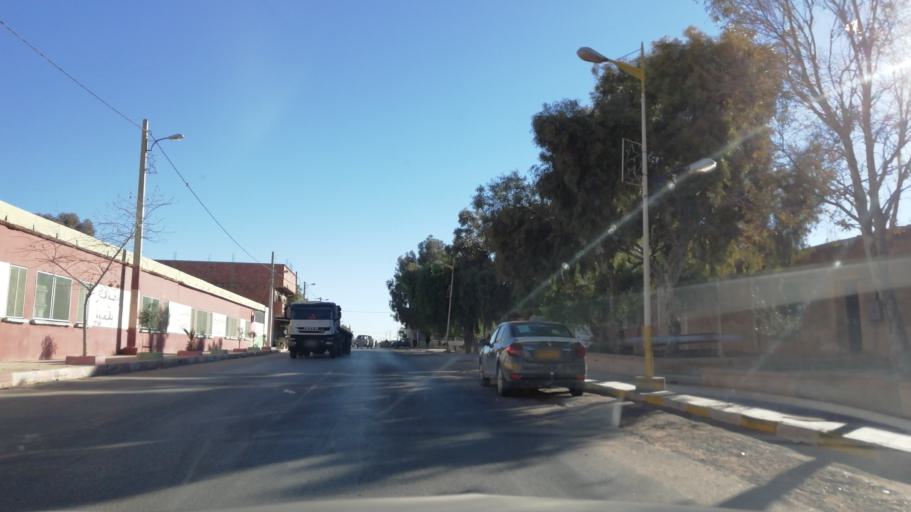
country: DZ
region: El Bayadh
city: El Bayadh
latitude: 33.8531
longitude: 0.6302
